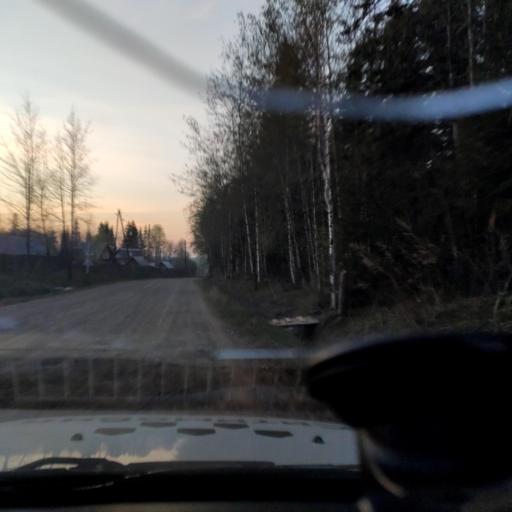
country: RU
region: Perm
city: Yug
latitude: 57.5890
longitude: 56.2045
